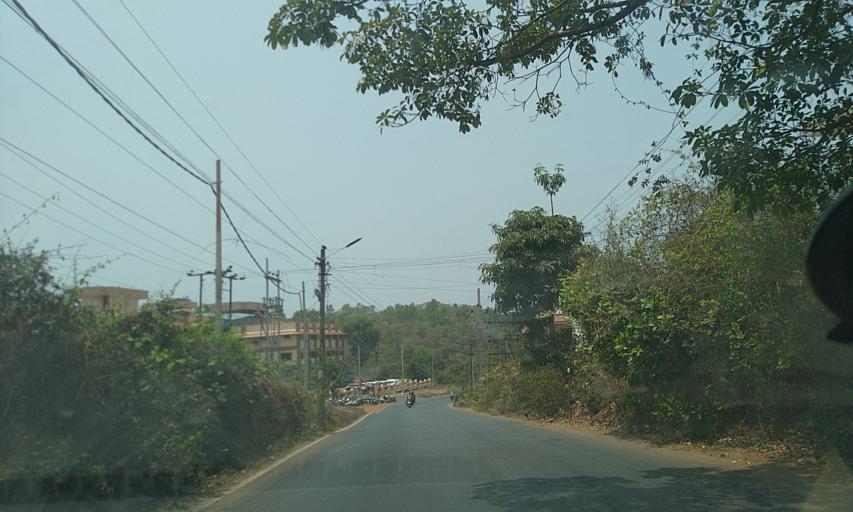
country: IN
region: Goa
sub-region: North Goa
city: Mapuca
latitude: 15.5952
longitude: 73.7964
